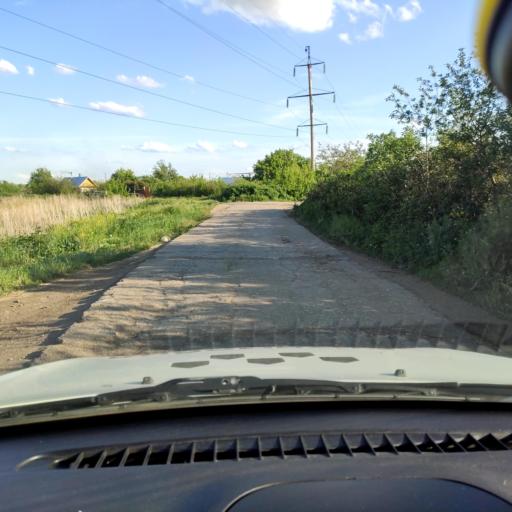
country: RU
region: Samara
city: Tol'yatti
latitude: 53.5904
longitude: 49.4359
